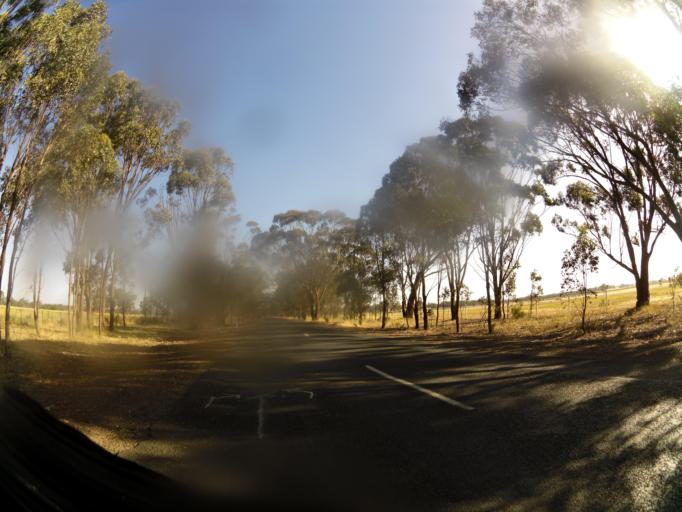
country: AU
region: Victoria
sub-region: Murrindindi
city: Kinglake West
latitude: -36.9759
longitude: 145.1101
